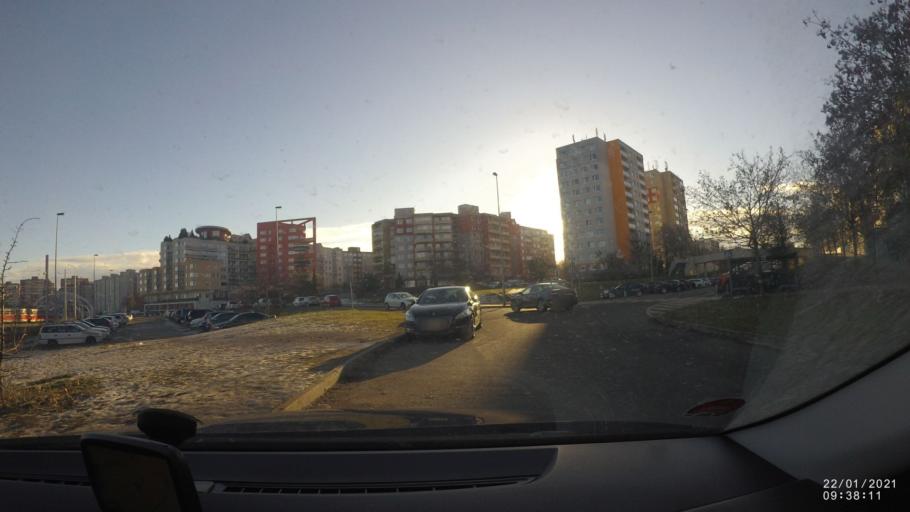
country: CZ
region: Praha
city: Branik
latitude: 50.0311
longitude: 14.3661
